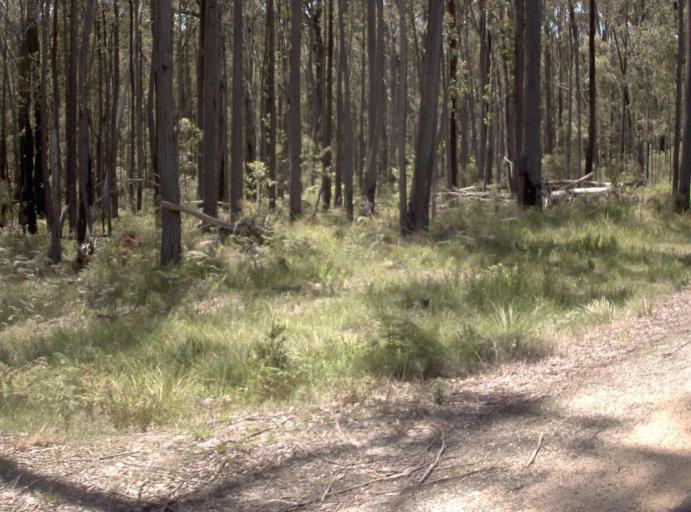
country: AU
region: Victoria
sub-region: East Gippsland
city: Lakes Entrance
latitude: -37.6710
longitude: 148.7963
